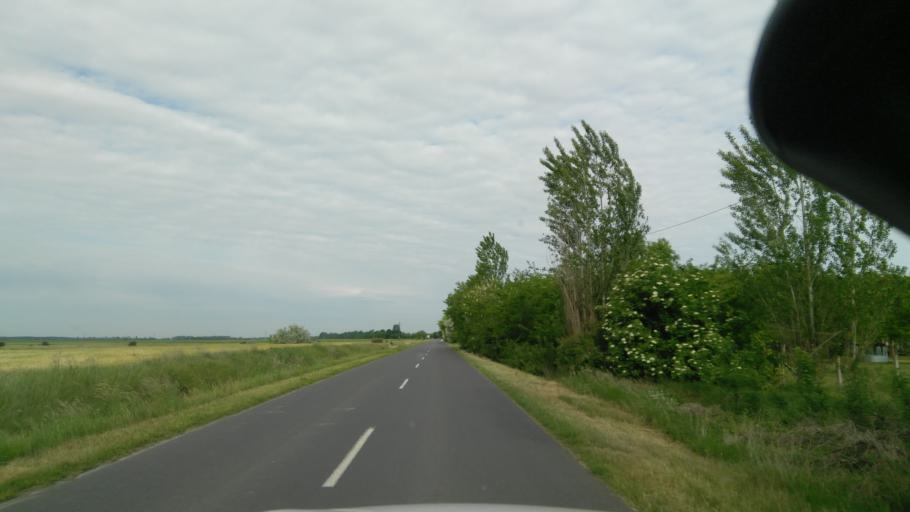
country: HU
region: Bekes
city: Ketegyhaza
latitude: 46.5396
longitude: 21.1562
